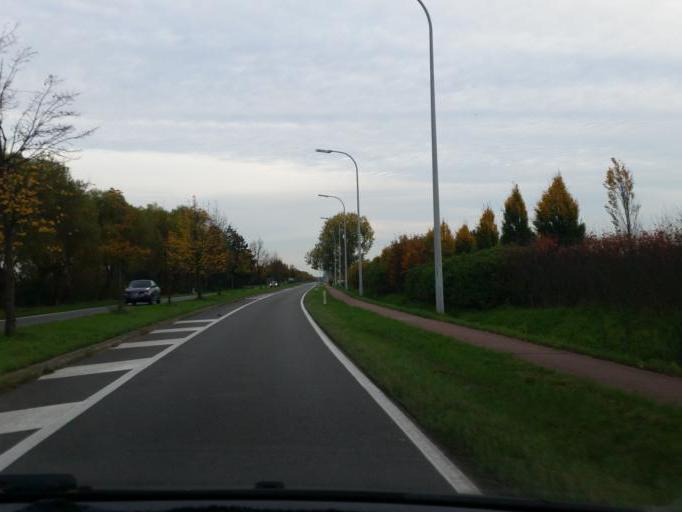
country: BE
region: Flanders
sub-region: Provincie Antwerpen
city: Lier
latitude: 51.1063
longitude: 4.6030
